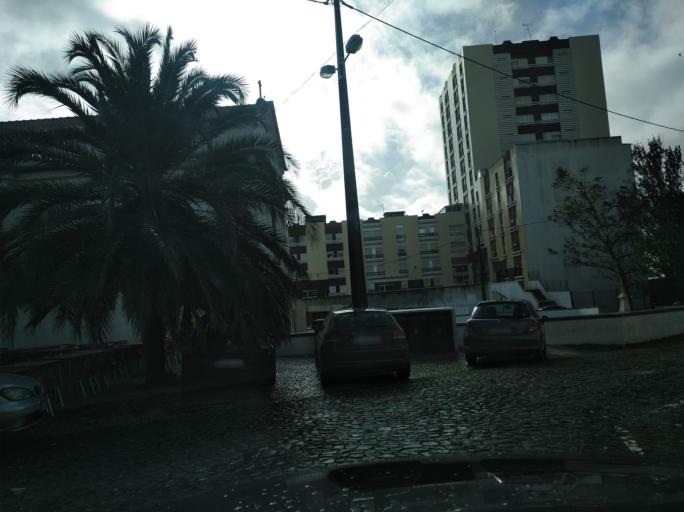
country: PT
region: Lisbon
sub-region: Loures
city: Moscavide
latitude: 38.7690
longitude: -9.1070
